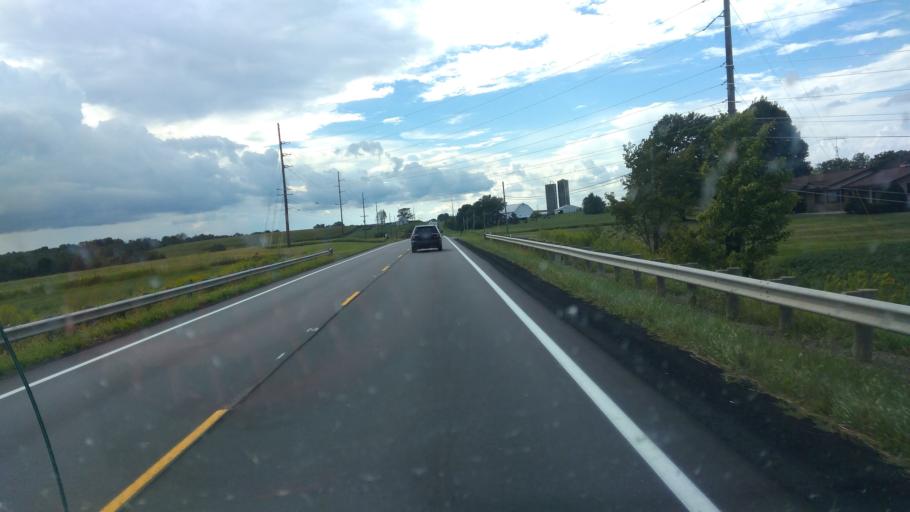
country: US
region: Ohio
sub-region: Holmes County
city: Millersburg
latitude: 40.5711
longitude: -81.9869
